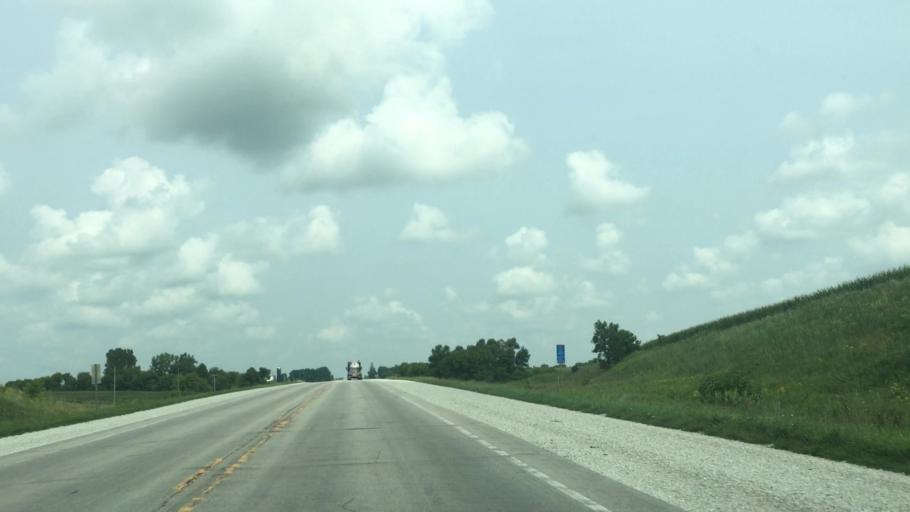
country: US
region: Minnesota
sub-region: Fillmore County
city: Harmony
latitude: 43.4609
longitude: -91.8697
